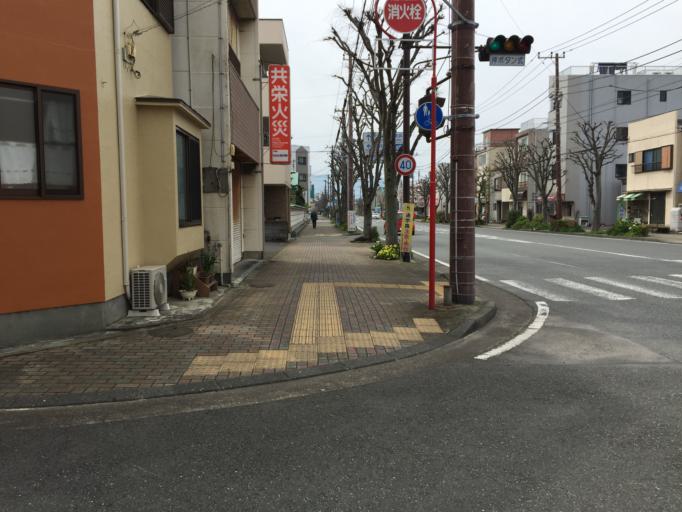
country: JP
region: Shizuoka
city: Numazu
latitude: 35.0918
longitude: 138.8568
